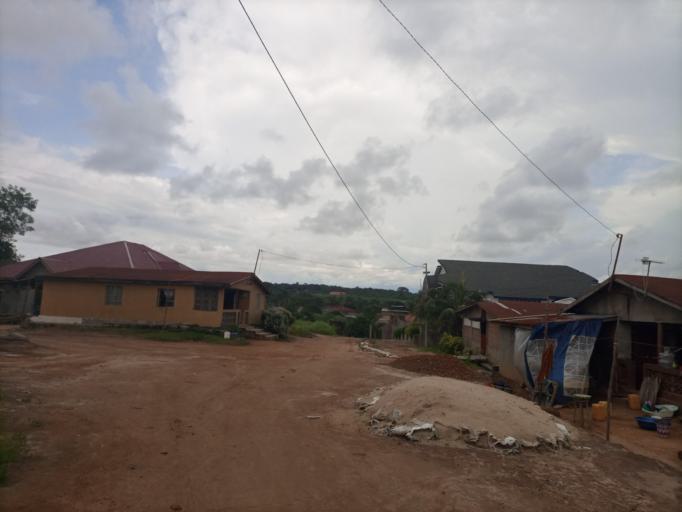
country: SL
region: Northern Province
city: Masoyila
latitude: 8.6046
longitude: -13.1714
